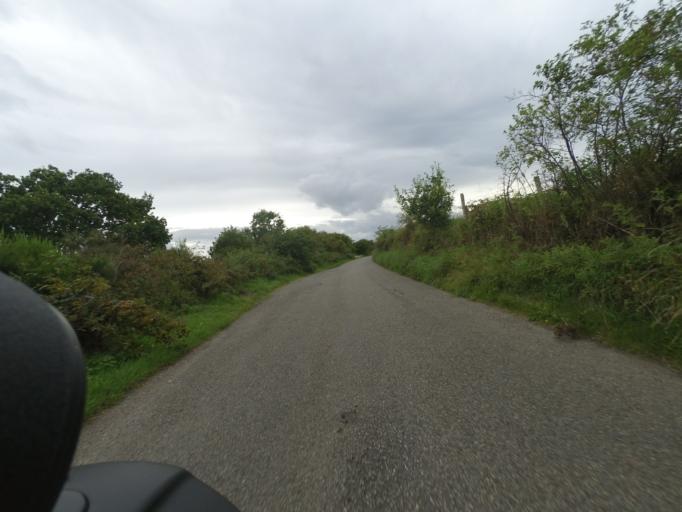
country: GB
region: Scotland
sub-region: Highland
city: Inverness
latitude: 57.5047
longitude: -4.2744
